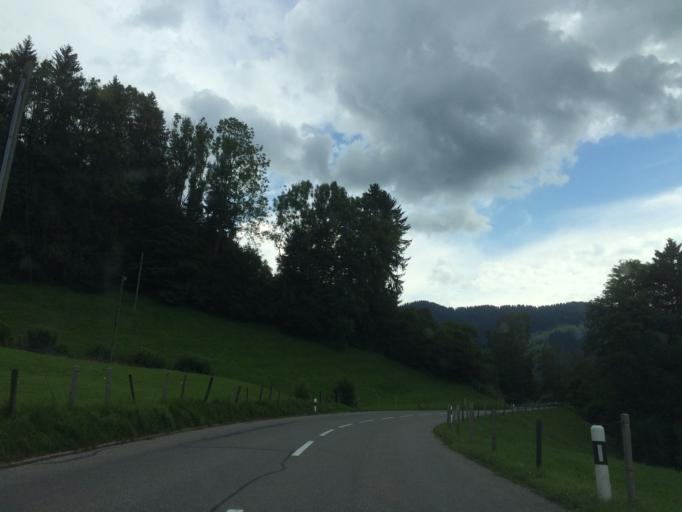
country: CH
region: Saint Gallen
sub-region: Wahlkreis Toggenburg
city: Krummenau
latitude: 47.2135
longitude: 9.2166
